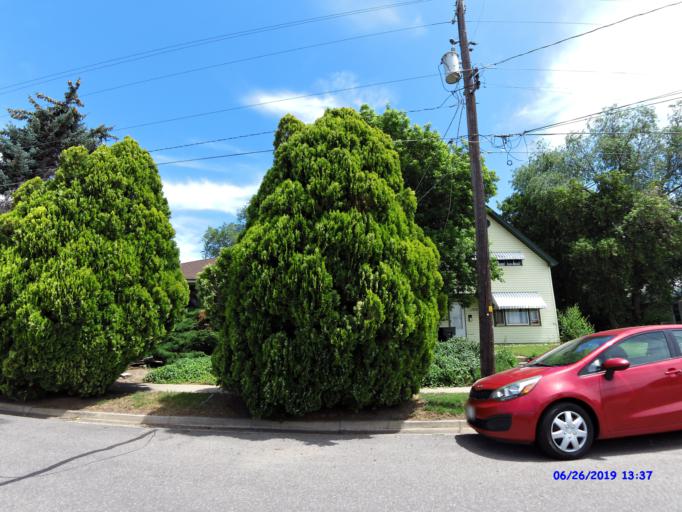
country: US
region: Utah
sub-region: Weber County
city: South Ogden
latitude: 41.2058
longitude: -111.9639
